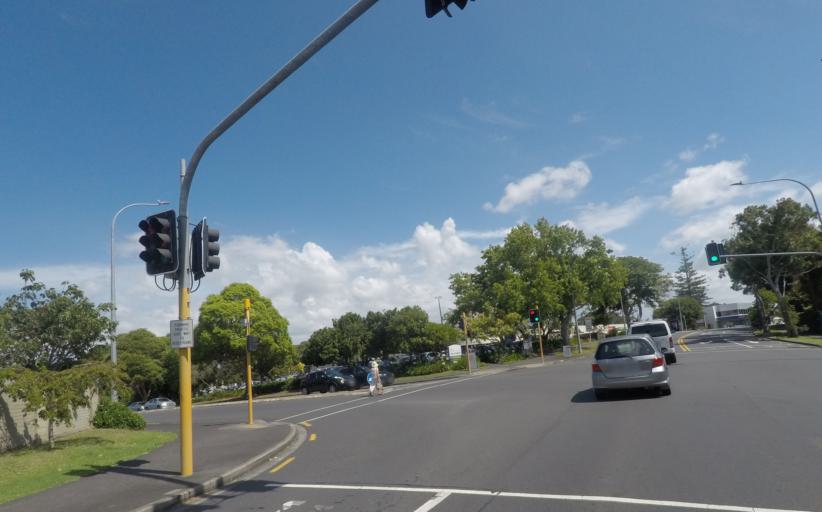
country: NZ
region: Auckland
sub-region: Auckland
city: Tamaki
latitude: -36.8748
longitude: 174.8282
